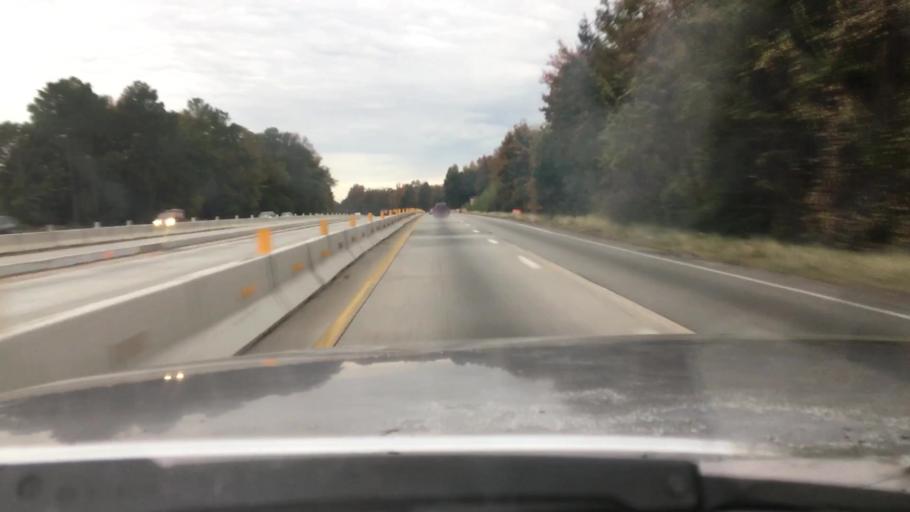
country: US
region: South Carolina
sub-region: Lexington County
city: Oak Grove
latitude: 33.9915
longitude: -81.1851
